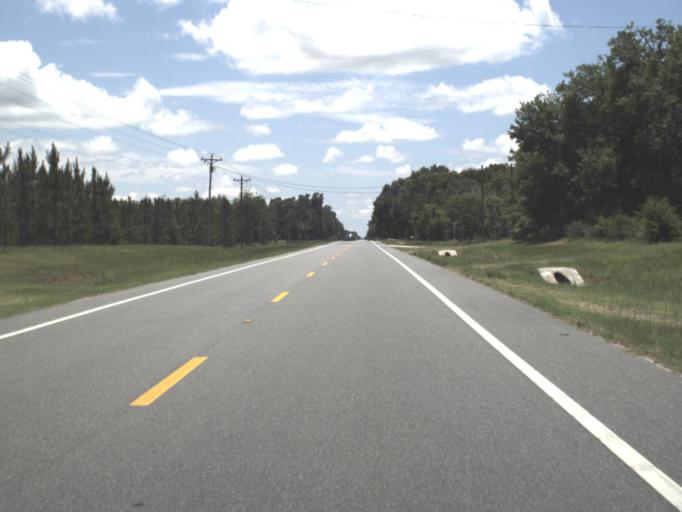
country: US
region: Florida
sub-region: Lafayette County
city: Mayo
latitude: 29.9285
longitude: -82.9499
